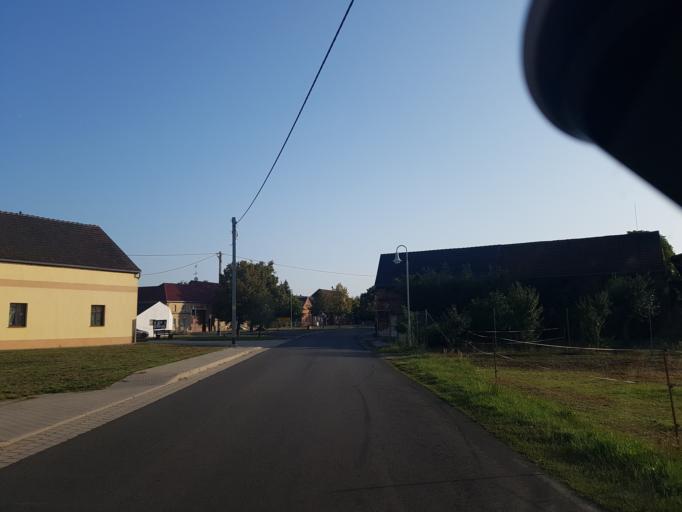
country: DE
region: Saxony-Anhalt
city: Holzdorf
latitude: 51.8299
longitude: 13.1231
